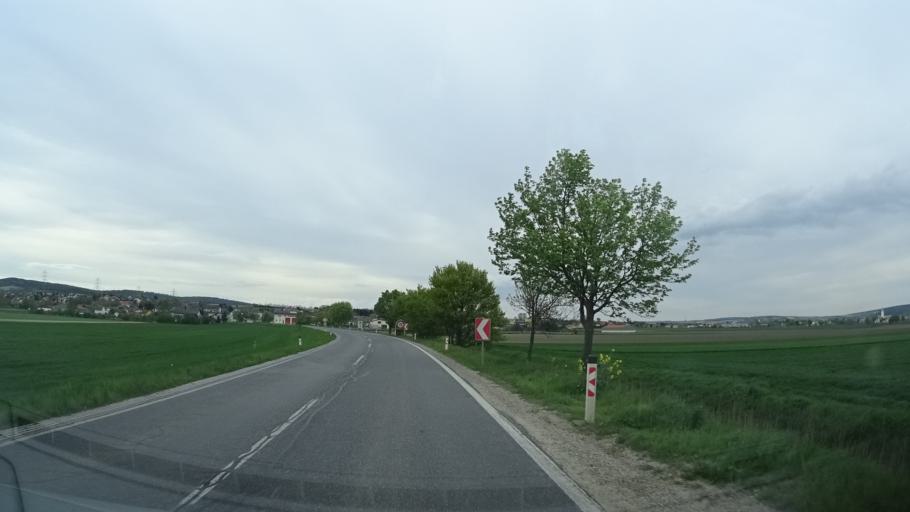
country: AT
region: Lower Austria
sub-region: Politischer Bezirk Korneuburg
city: Harmannsdorf
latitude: 48.3762
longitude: 16.3611
